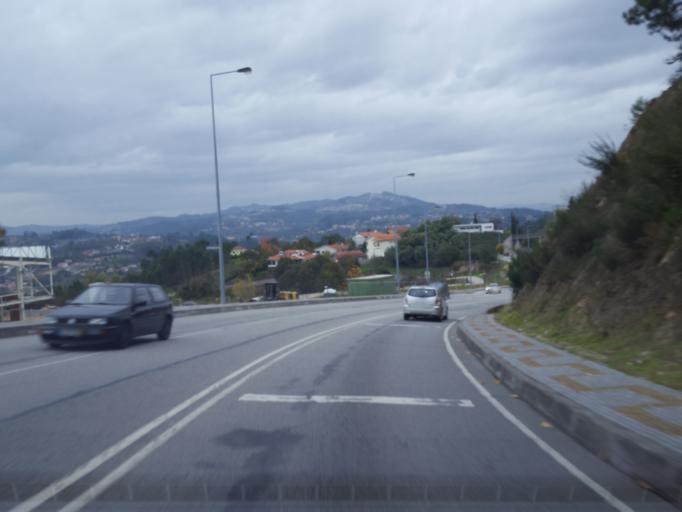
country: PT
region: Porto
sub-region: Marco de Canaveses
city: Marco de Canavezes
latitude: 41.1856
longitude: -8.1567
